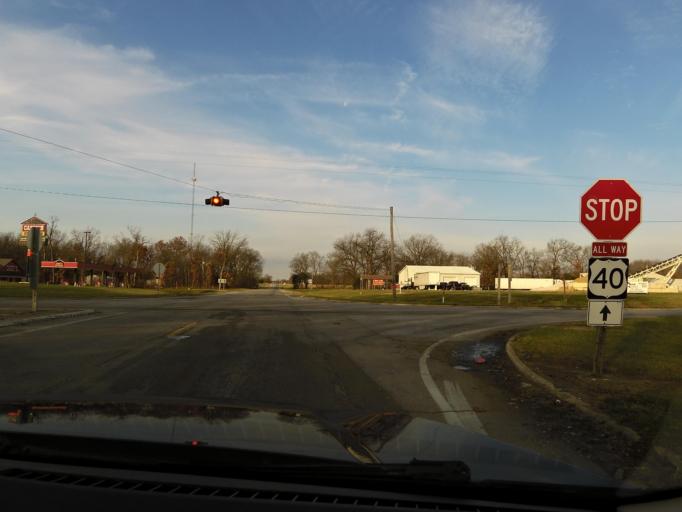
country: US
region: Illinois
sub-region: Bond County
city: Greenville
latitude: 38.9185
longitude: -89.2687
